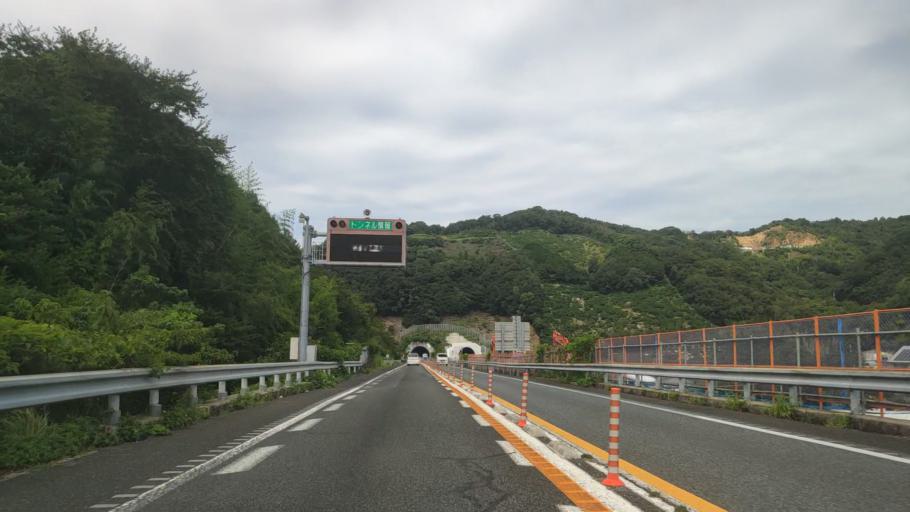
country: JP
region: Wakayama
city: Gobo
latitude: 33.9958
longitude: 135.1974
